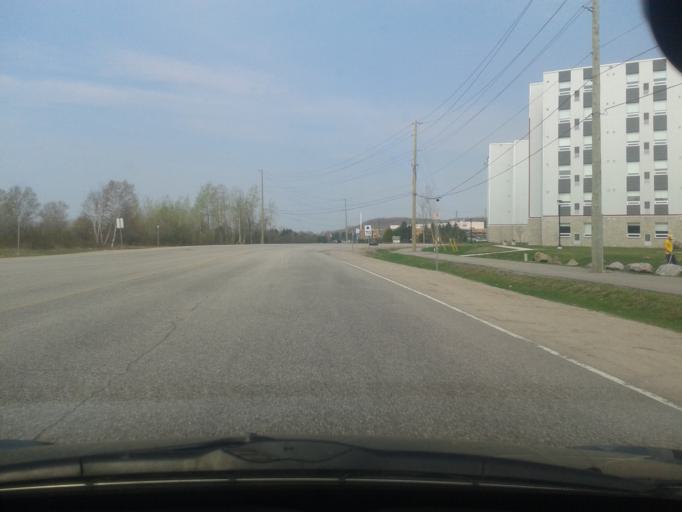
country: CA
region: Ontario
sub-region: Nipissing District
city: North Bay
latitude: 46.3341
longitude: -79.4892
